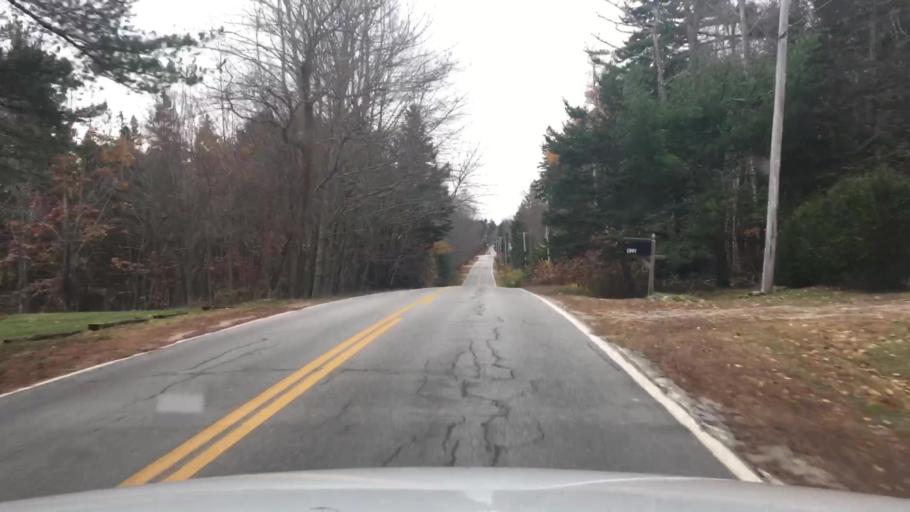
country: US
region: Maine
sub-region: Hancock County
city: Sedgwick
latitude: 44.3194
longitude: -68.5707
